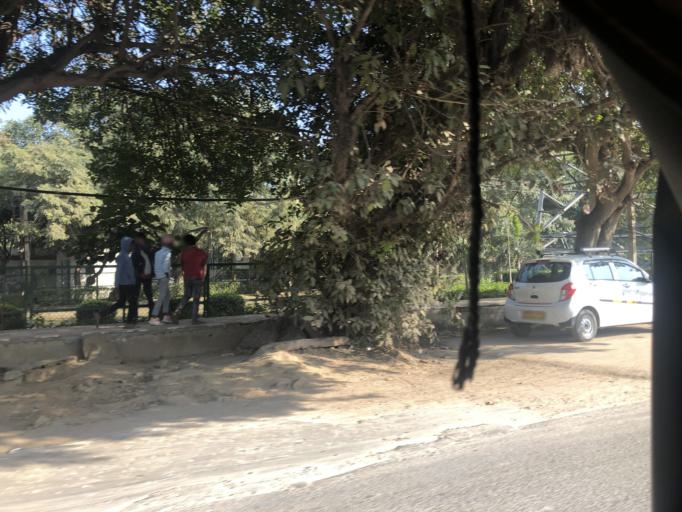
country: IN
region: Haryana
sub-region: Gurgaon
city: Gurgaon
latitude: 28.4582
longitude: 77.0742
